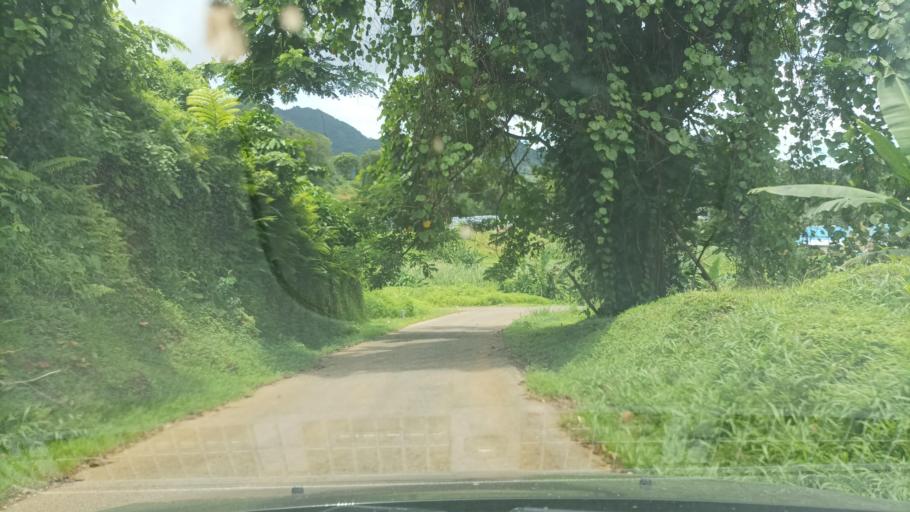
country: FM
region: Kosrae
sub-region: Lelu Municipality
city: Tofol
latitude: 5.3234
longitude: 163.0070
